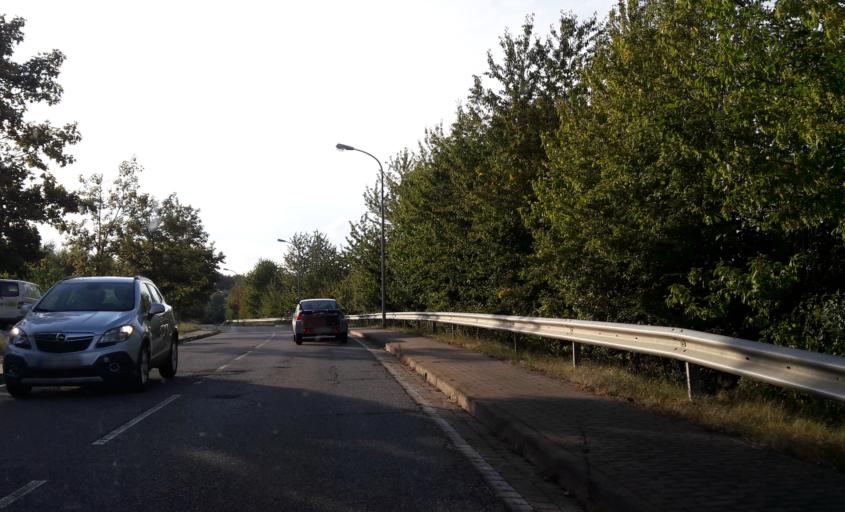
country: DE
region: Rheinland-Pfalz
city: Zell
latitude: 50.0325
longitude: 7.1640
